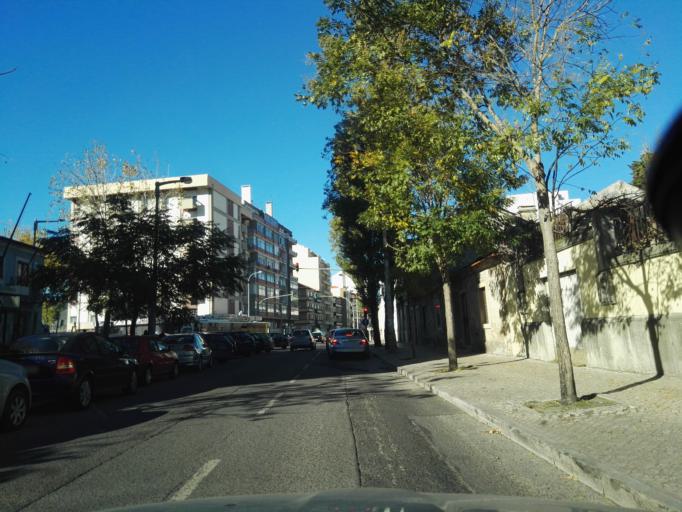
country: PT
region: Lisbon
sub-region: Odivelas
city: Olival do Basto
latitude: 38.7622
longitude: -9.1563
